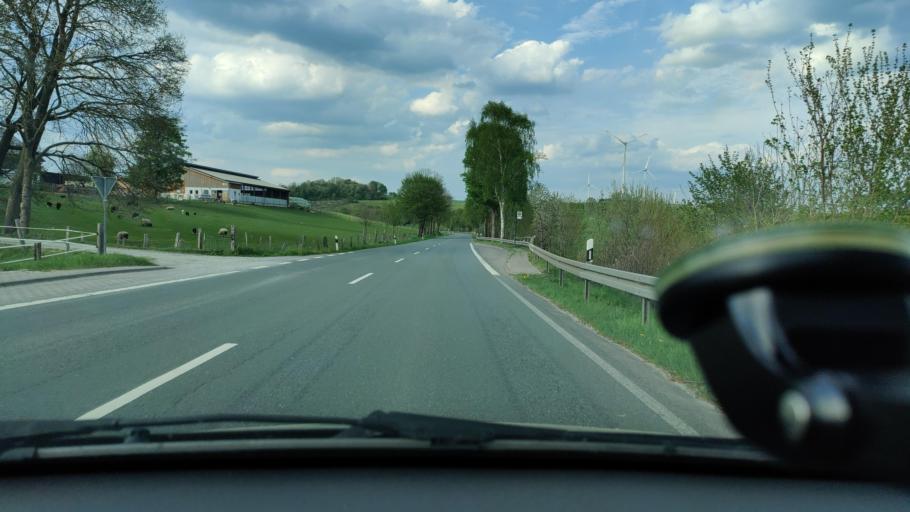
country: DE
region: North Rhine-Westphalia
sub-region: Regierungsbezirk Arnsberg
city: Brilon
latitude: 51.4151
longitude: 8.5786
